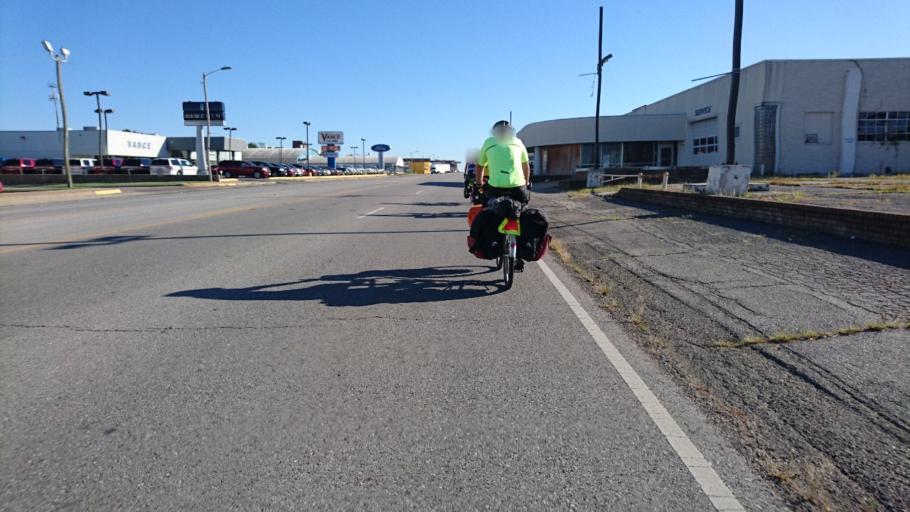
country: US
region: Oklahoma
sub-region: Ottawa County
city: Miami
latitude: 36.8834
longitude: -94.8777
